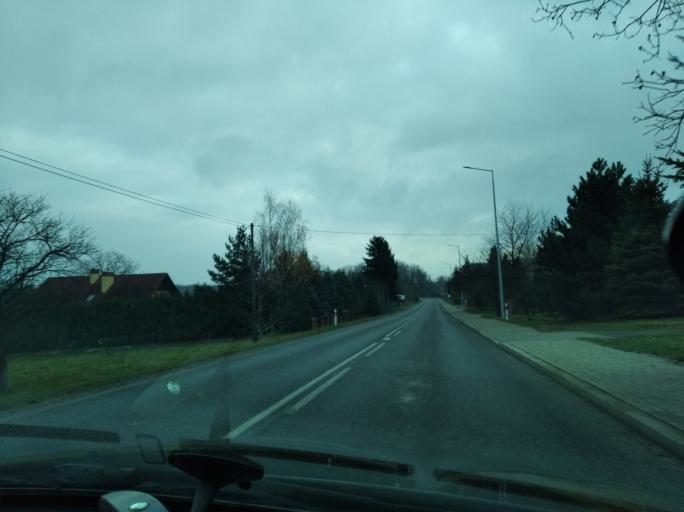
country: PL
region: Subcarpathian Voivodeship
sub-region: Powiat przeworski
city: Sietesz
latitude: 50.0022
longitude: 22.3498
